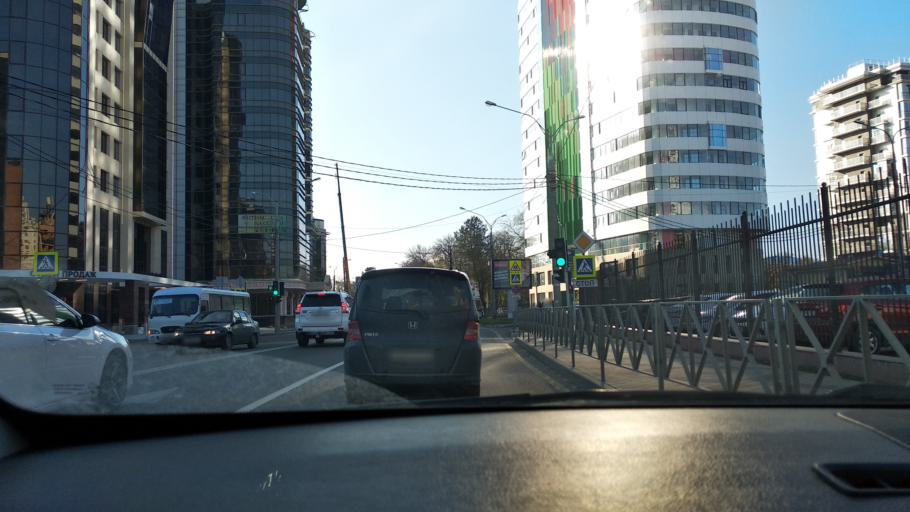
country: RU
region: Krasnodarskiy
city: Krasnodar
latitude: 45.0182
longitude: 38.9594
